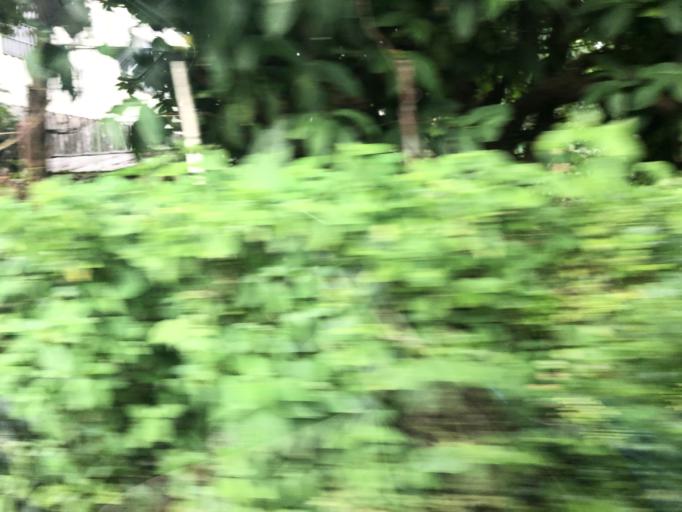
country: TW
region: Taiwan
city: Daxi
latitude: 24.9207
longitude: 121.3638
